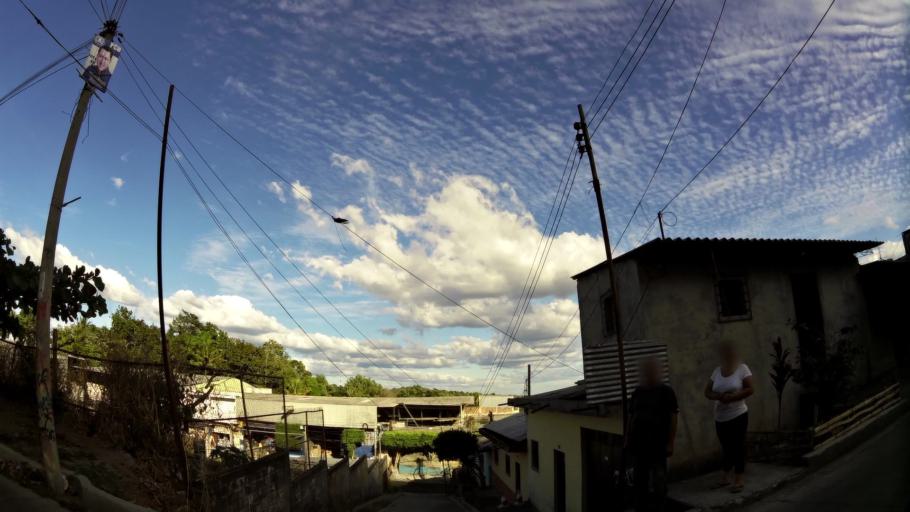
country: SV
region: Cuscatlan
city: Cojutepeque
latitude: 13.7161
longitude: -88.9332
